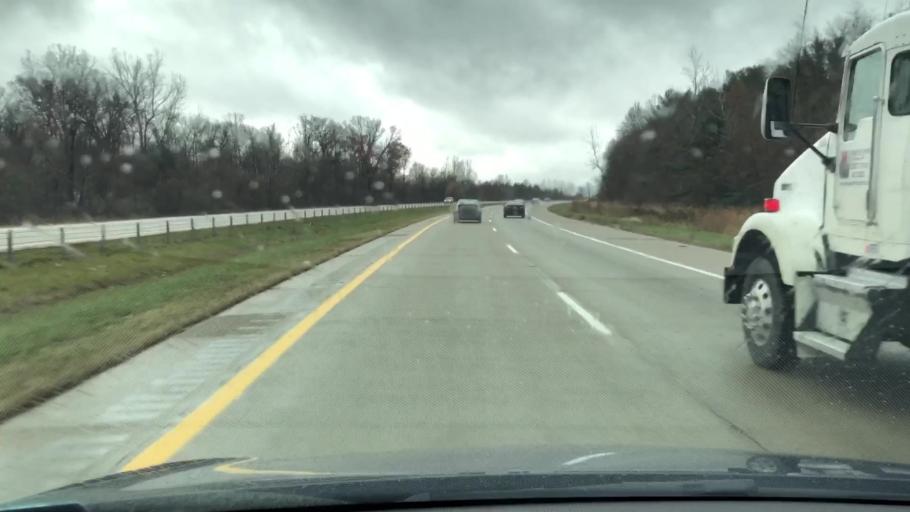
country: US
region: Michigan
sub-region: Monroe County
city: Lambertville
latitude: 41.8050
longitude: -83.6839
